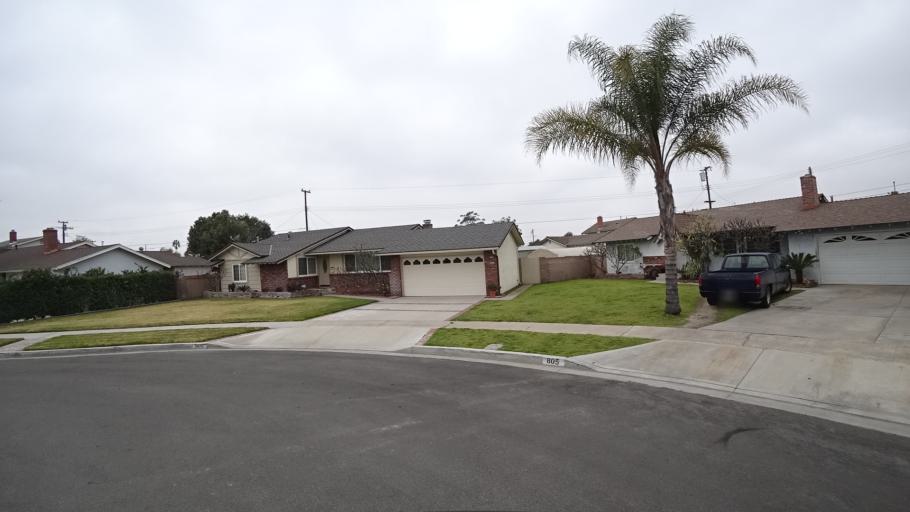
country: US
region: California
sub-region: Orange County
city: Stanton
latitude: 33.8208
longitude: -118.0066
